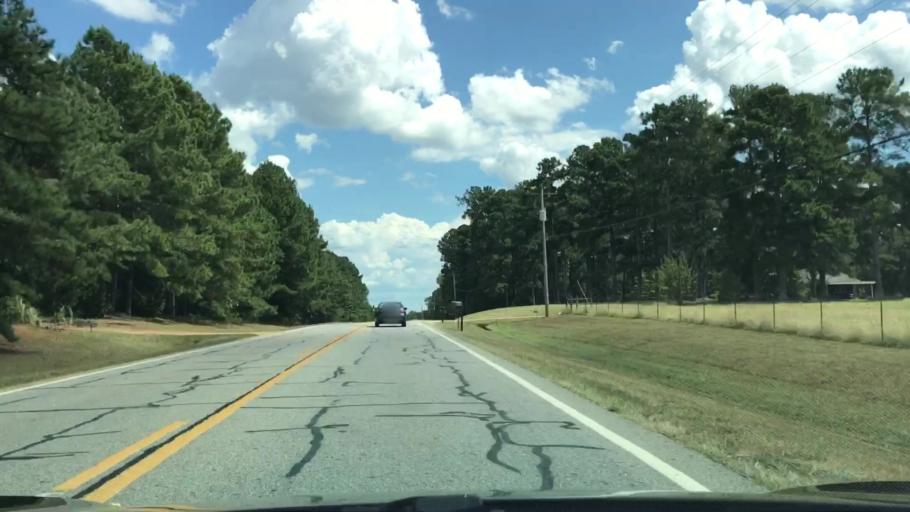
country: US
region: Georgia
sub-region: Oconee County
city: Watkinsville
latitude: 33.8093
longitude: -83.3523
